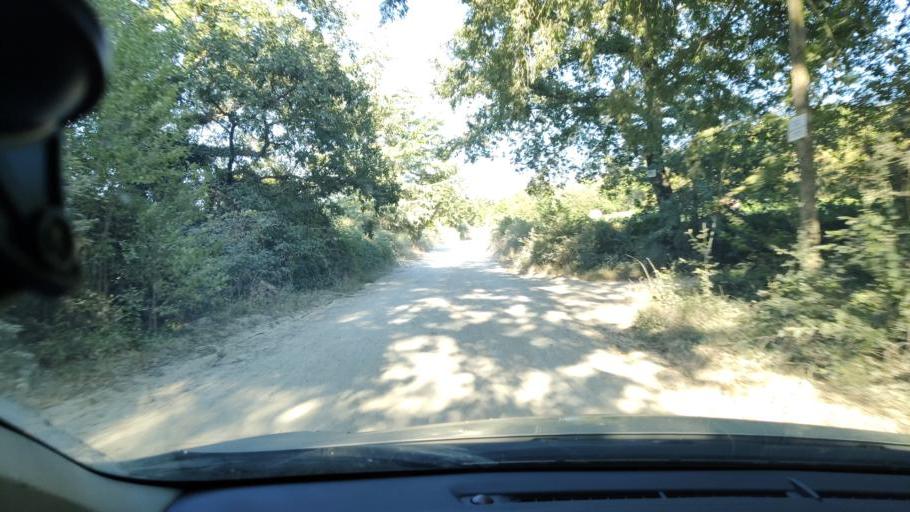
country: IT
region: Umbria
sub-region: Provincia di Terni
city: Penna in Teverina
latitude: 42.5399
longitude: 12.3670
